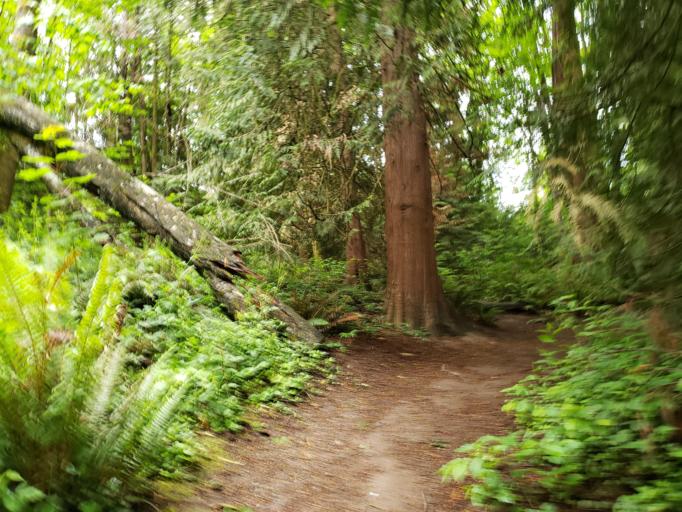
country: US
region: Oregon
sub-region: Washington County
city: Garden Home-Whitford
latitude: 45.4694
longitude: -122.7356
